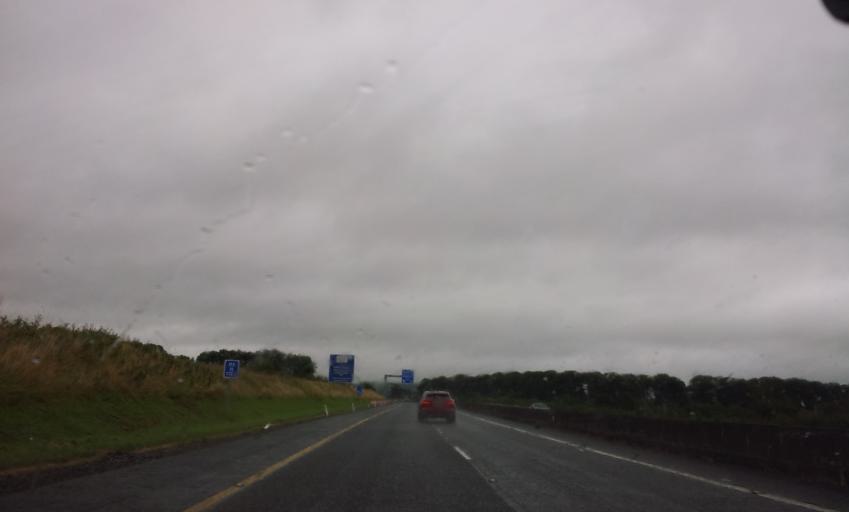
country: IE
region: Munster
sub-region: County Cork
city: Fermoy
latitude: 52.1543
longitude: -8.2663
